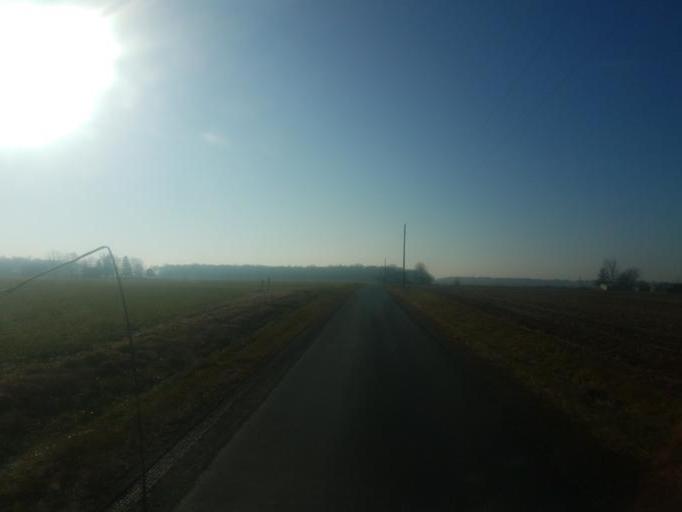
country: US
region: Ohio
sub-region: Crawford County
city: Bucyrus
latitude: 40.8168
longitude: -82.8784
